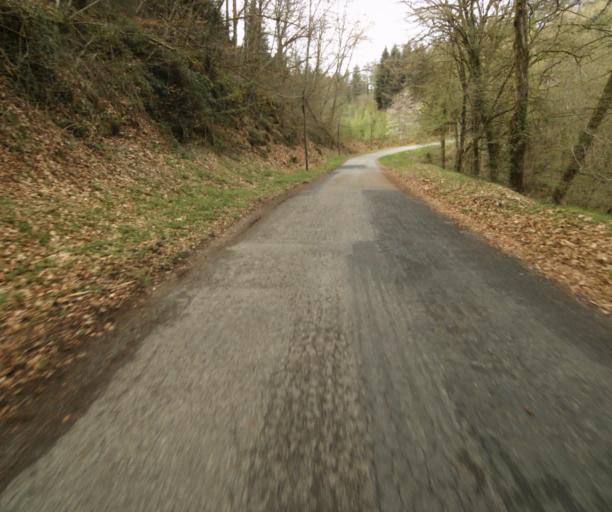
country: FR
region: Limousin
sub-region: Departement de la Correze
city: Argentat
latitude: 45.2030
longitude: 1.9619
